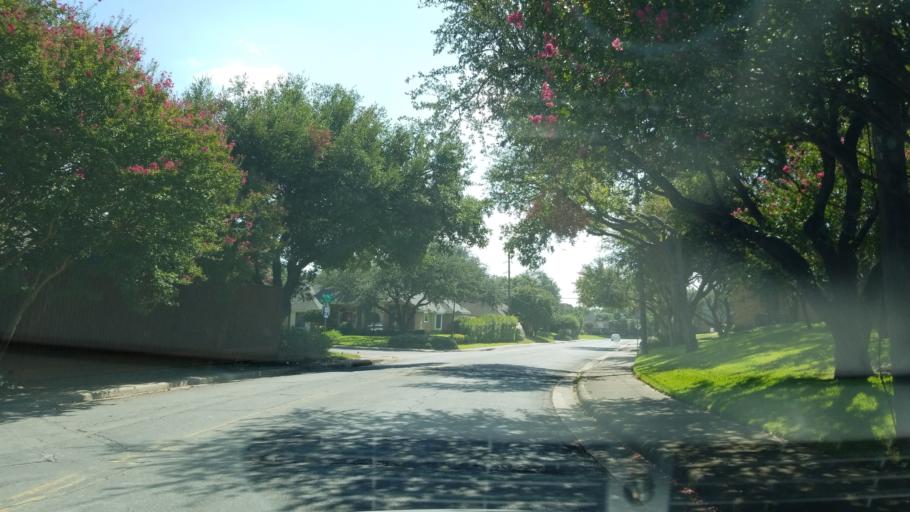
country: US
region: Texas
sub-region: Dallas County
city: Addison
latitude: 32.9555
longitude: -96.8015
